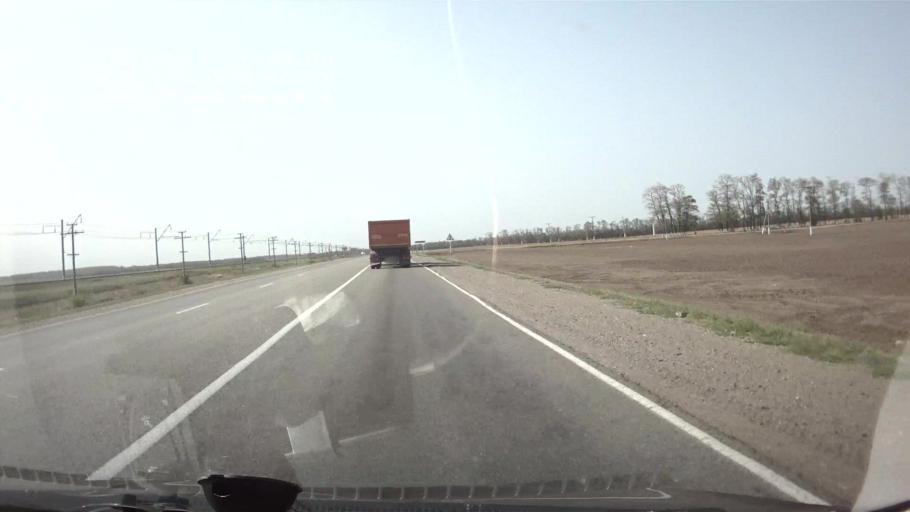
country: RU
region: Krasnodarskiy
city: Ladozhskaya
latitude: 45.3436
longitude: 39.9627
